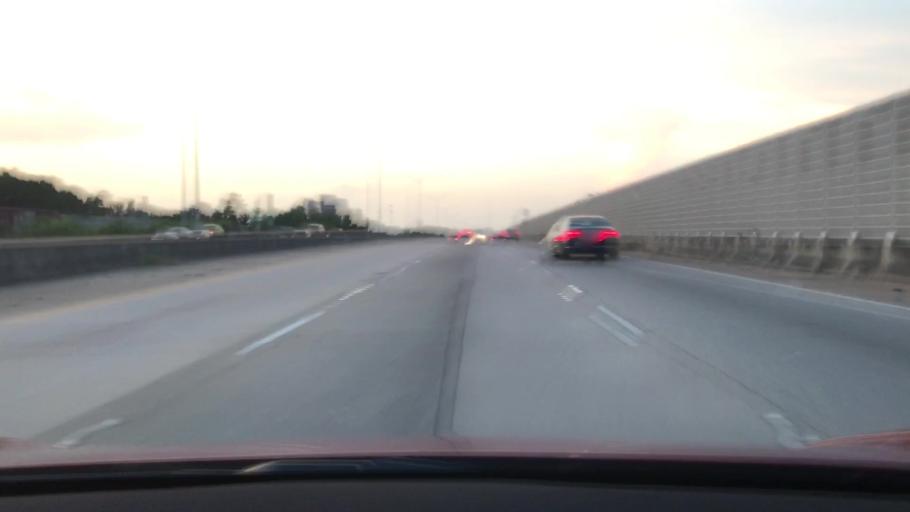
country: US
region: Louisiana
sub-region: Bossier Parish
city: Bossier City
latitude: 32.4676
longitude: -93.7552
